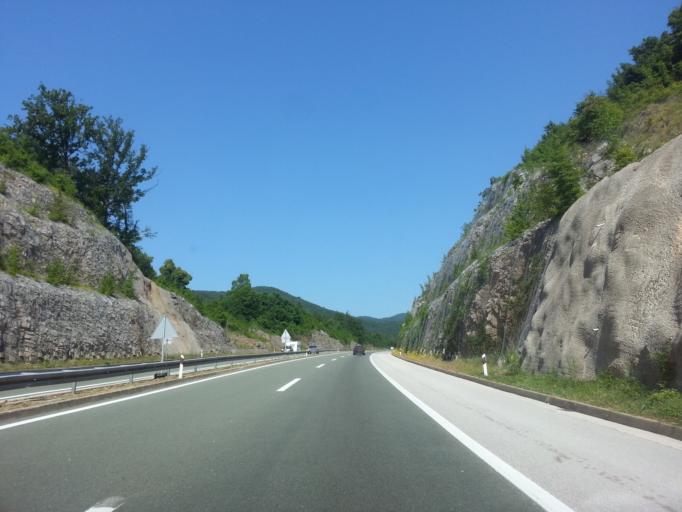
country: HR
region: Primorsko-Goranska
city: Matulji
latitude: 45.3795
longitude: 14.3110
